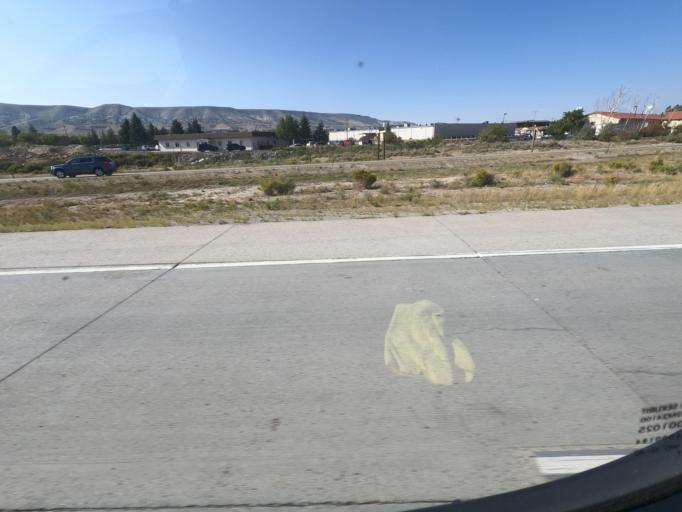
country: US
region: Wyoming
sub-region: Sweetwater County
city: Rock Springs
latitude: 41.5774
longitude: -109.2607
